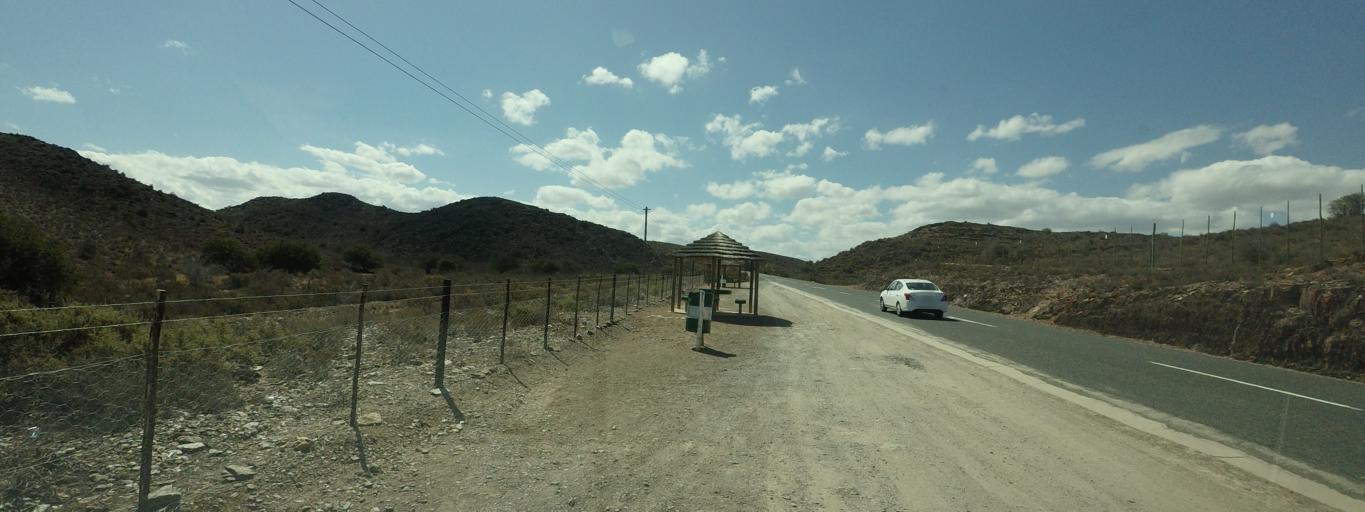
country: ZA
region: Western Cape
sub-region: Eden District Municipality
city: Ladismith
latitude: -33.7040
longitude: 20.9670
